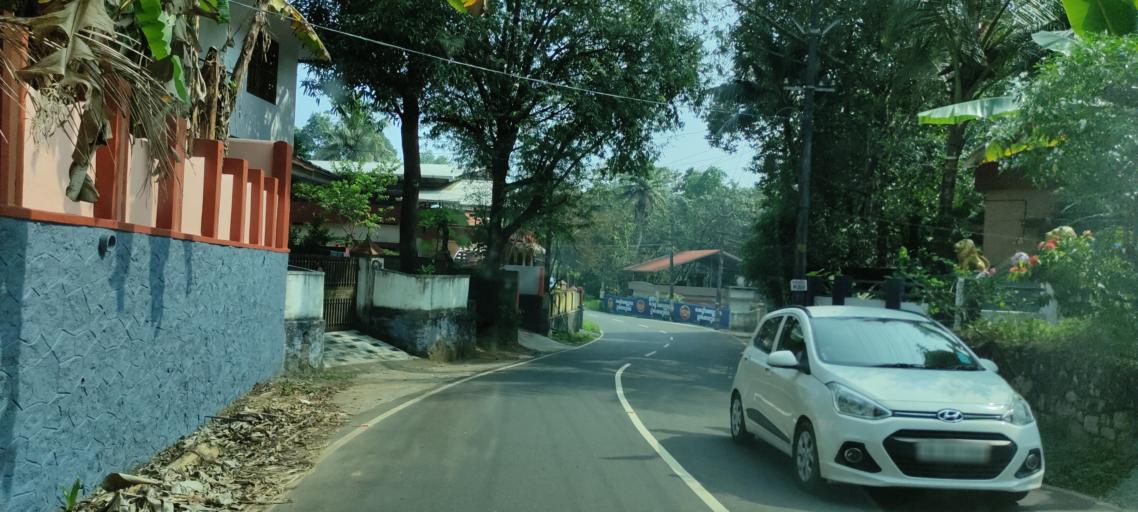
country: IN
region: Kerala
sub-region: Pattanamtitta
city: Adur
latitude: 9.2379
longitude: 76.6849
